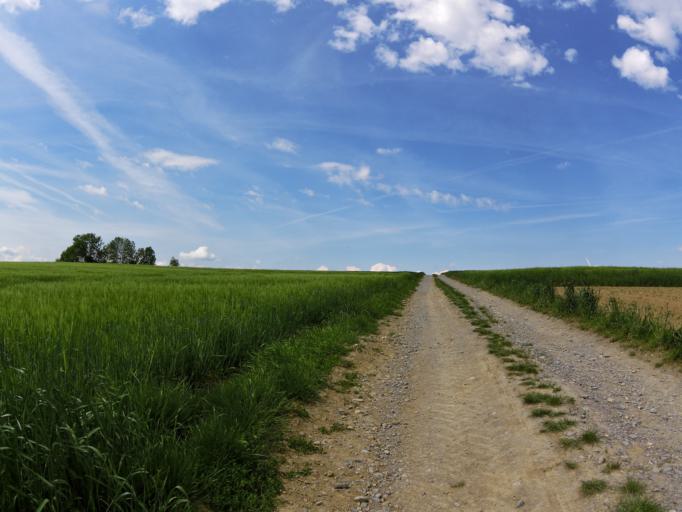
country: DE
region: Bavaria
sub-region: Regierungsbezirk Unterfranken
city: Theilheim
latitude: 49.7356
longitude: 10.0440
